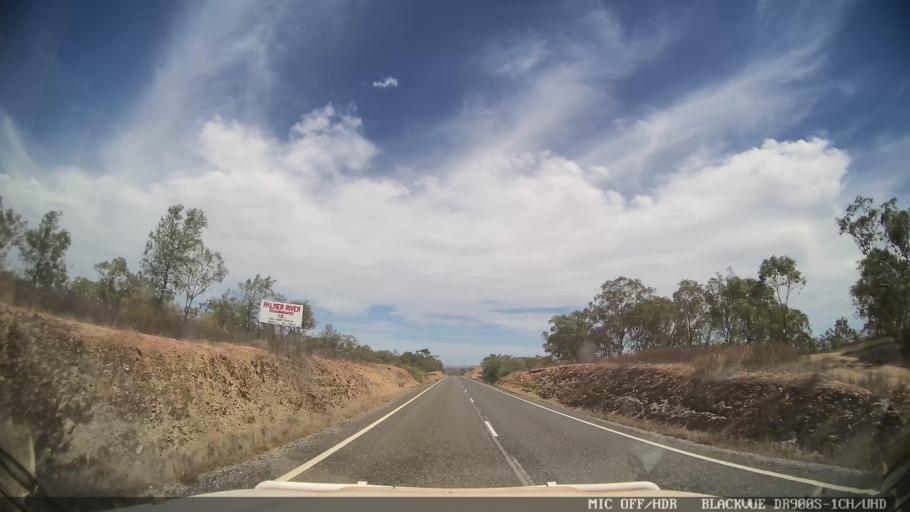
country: AU
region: Queensland
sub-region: Cook
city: Cooktown
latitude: -16.0285
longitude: 144.8084
